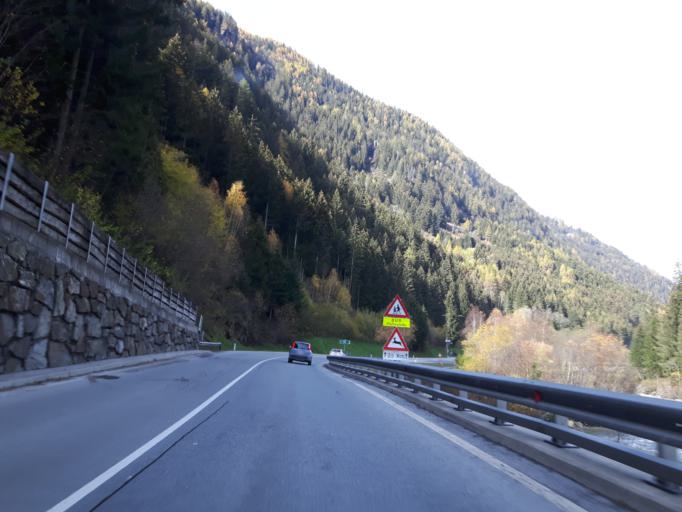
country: AT
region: Tyrol
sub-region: Politischer Bezirk Lienz
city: Hopfgarten in Defereggen
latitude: 46.9429
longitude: 12.5684
